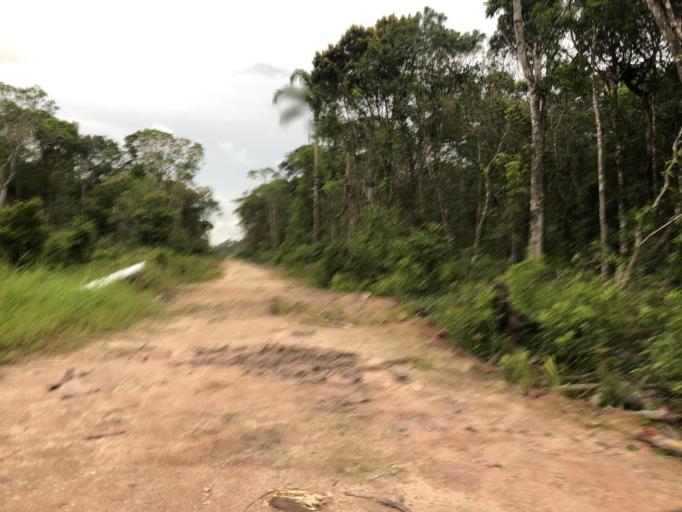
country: BR
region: Santa Catarina
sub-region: Sao Francisco Do Sul
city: Sao Francisco do Sul
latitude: -26.2150
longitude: -48.5349
